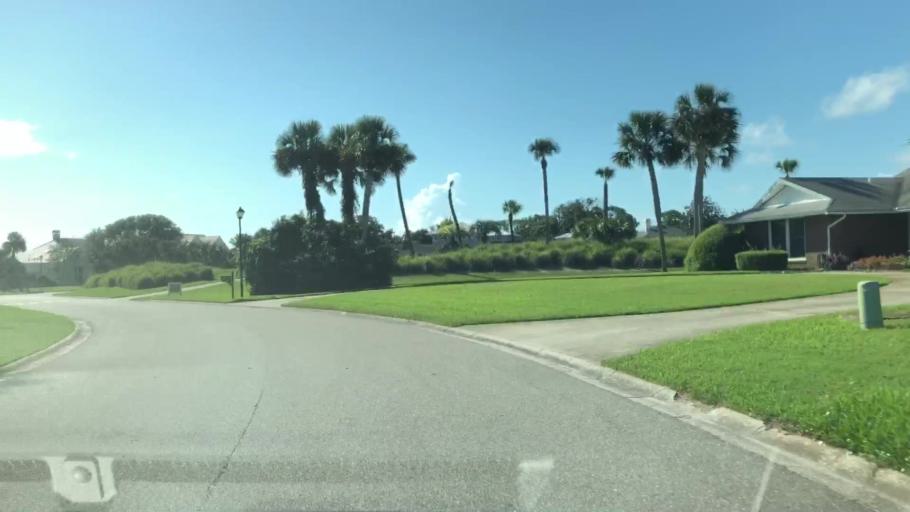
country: US
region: Florida
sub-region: Saint Johns County
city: Ponte Vedra Beach
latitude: 30.2336
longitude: -81.3836
